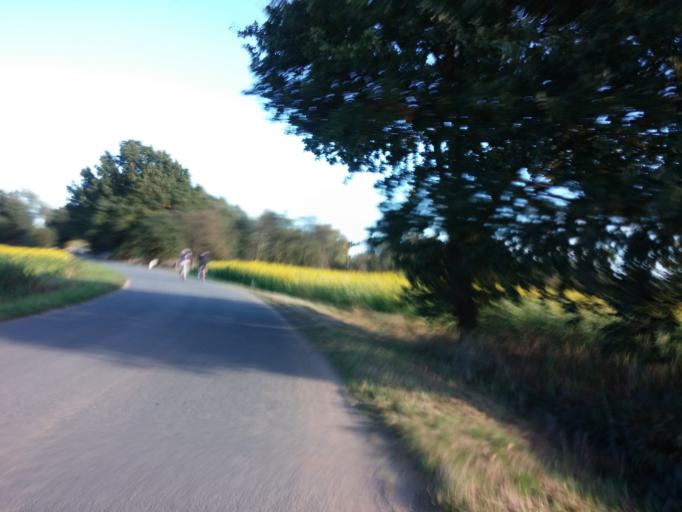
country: DE
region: North Rhine-Westphalia
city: Dorsten
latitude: 51.6339
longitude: 7.0257
